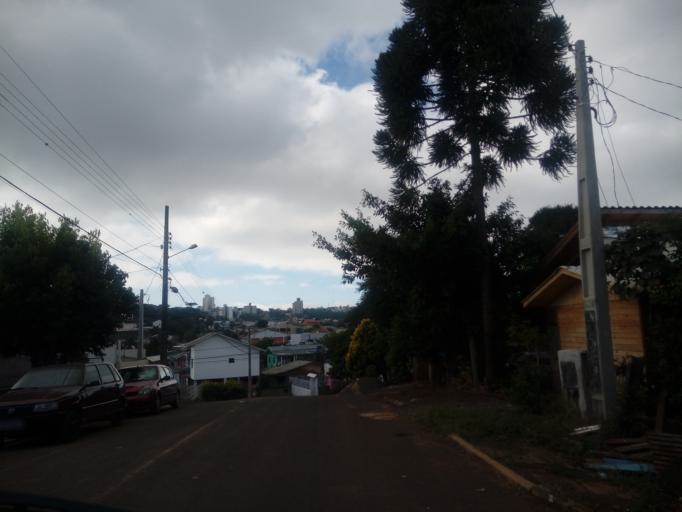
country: BR
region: Santa Catarina
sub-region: Chapeco
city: Chapeco
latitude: -27.1161
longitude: -52.6212
